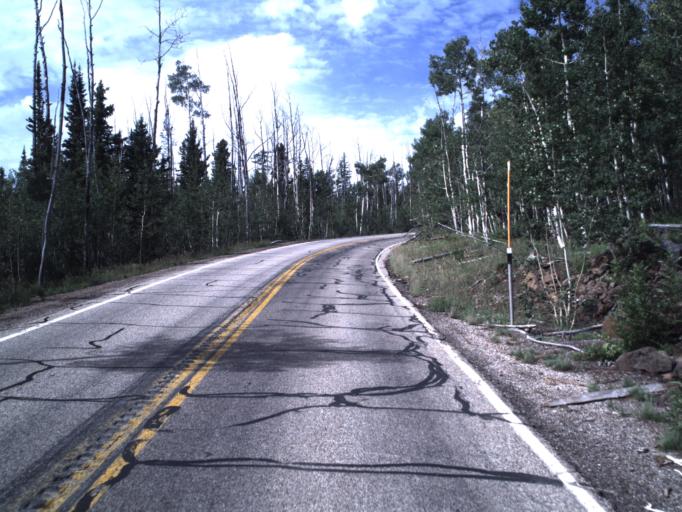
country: US
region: Utah
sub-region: Iron County
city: Parowan
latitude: 37.5189
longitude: -112.7093
